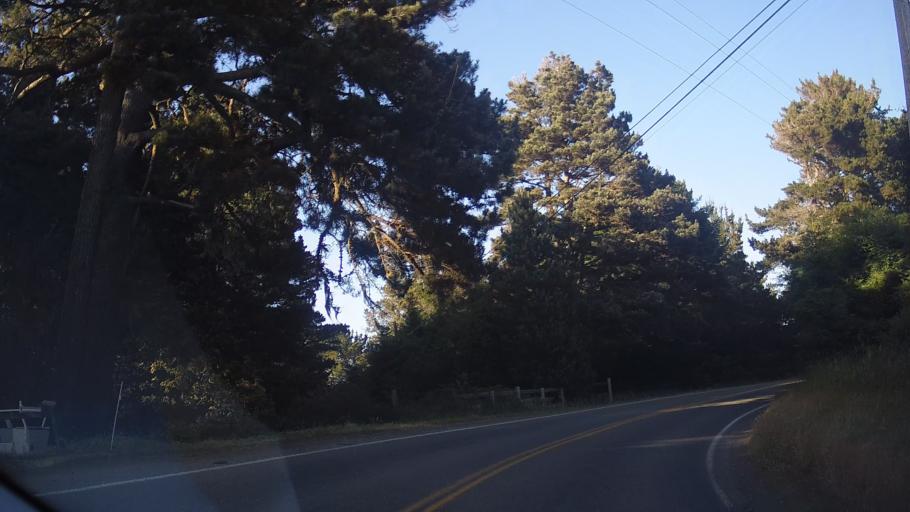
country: US
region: California
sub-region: Mendocino County
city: Fort Bragg
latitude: 39.4984
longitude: -123.7787
